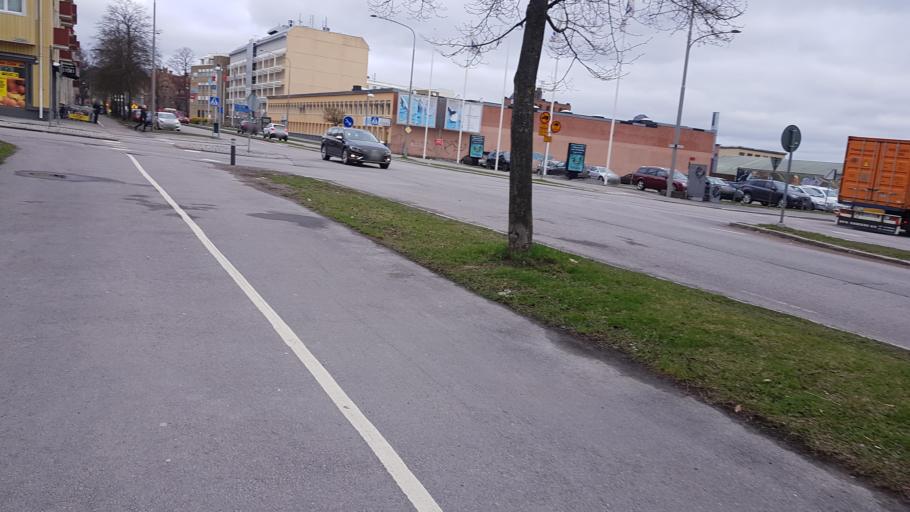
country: SE
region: OEstergoetland
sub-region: Norrkopings Kommun
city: Norrkoping
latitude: 58.5900
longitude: 16.2031
